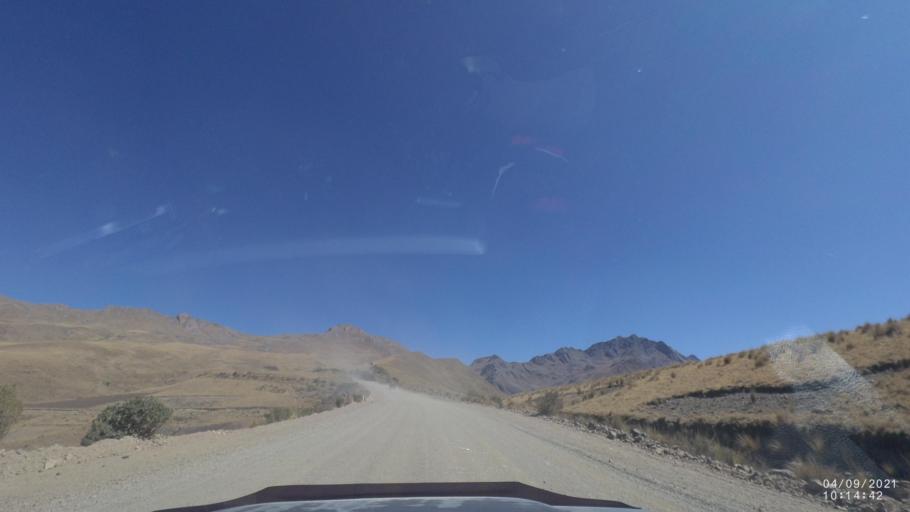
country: BO
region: Cochabamba
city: Sipe Sipe
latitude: -17.3285
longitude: -66.4105
